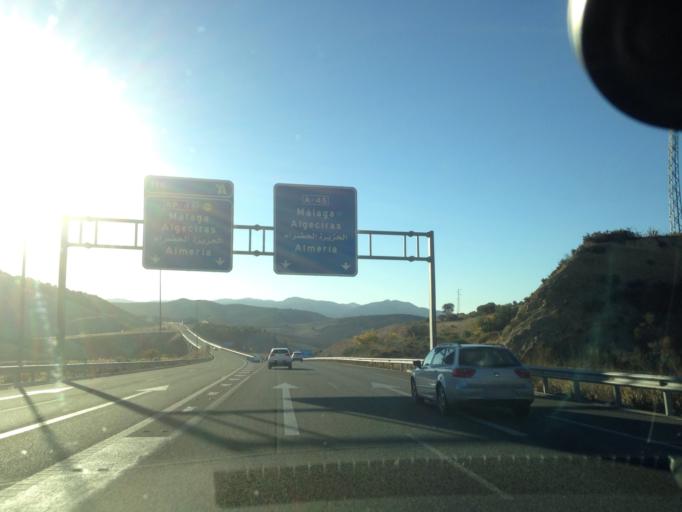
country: ES
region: Andalusia
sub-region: Provincia de Malaga
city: Casabermeja
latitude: 36.9508
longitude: -4.4448
